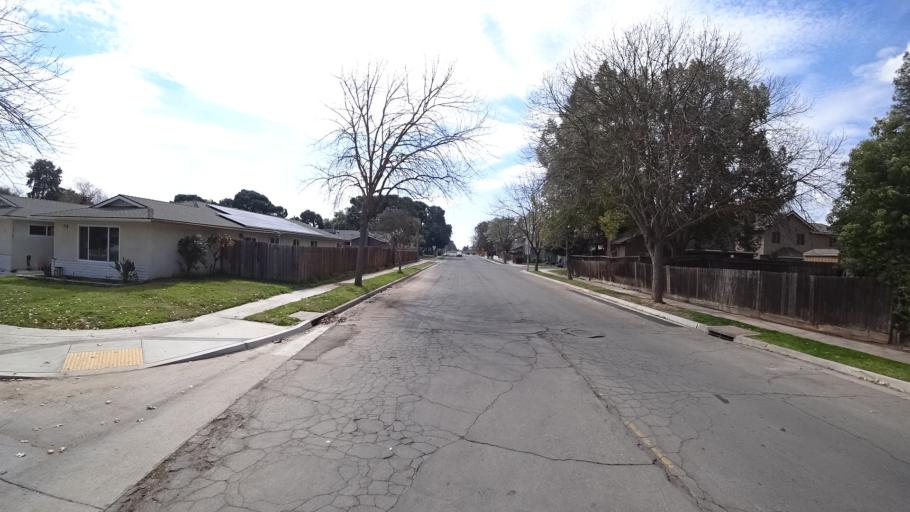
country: US
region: California
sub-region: Fresno County
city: Fresno
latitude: 36.8183
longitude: -119.8535
